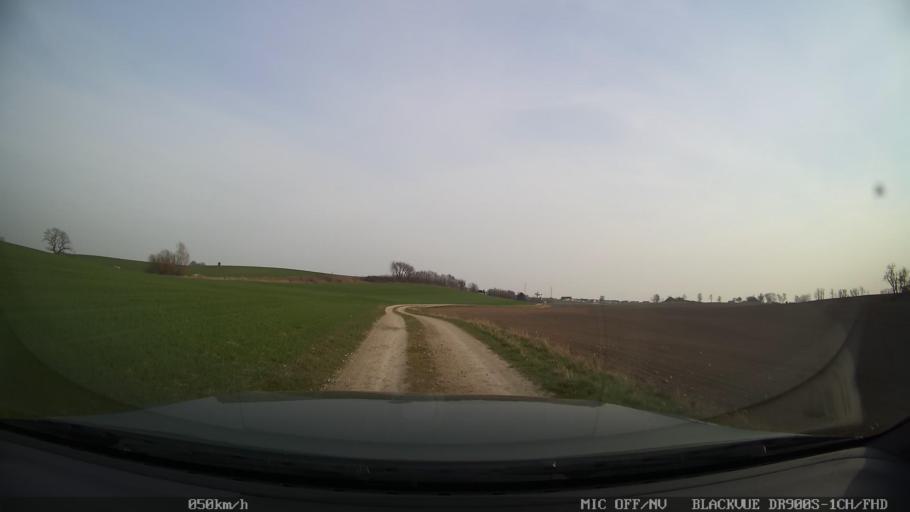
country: SE
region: Skane
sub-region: Ystads Kommun
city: Ystad
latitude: 55.4554
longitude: 13.7918
